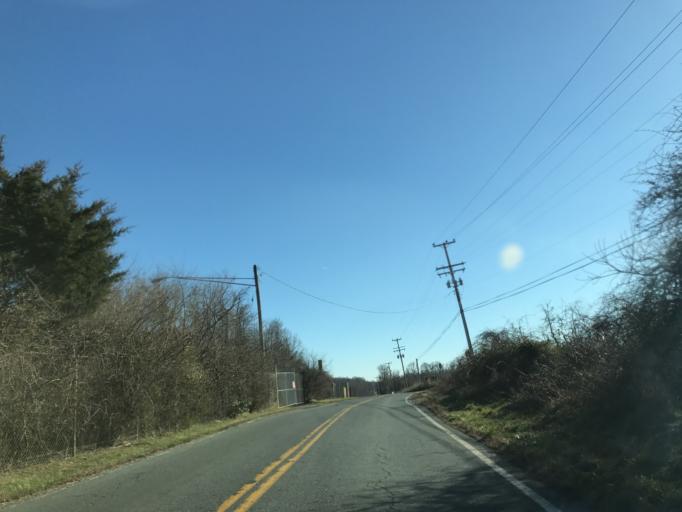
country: US
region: Maryland
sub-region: Harford County
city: Perryman
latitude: 39.4383
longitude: -76.2160
